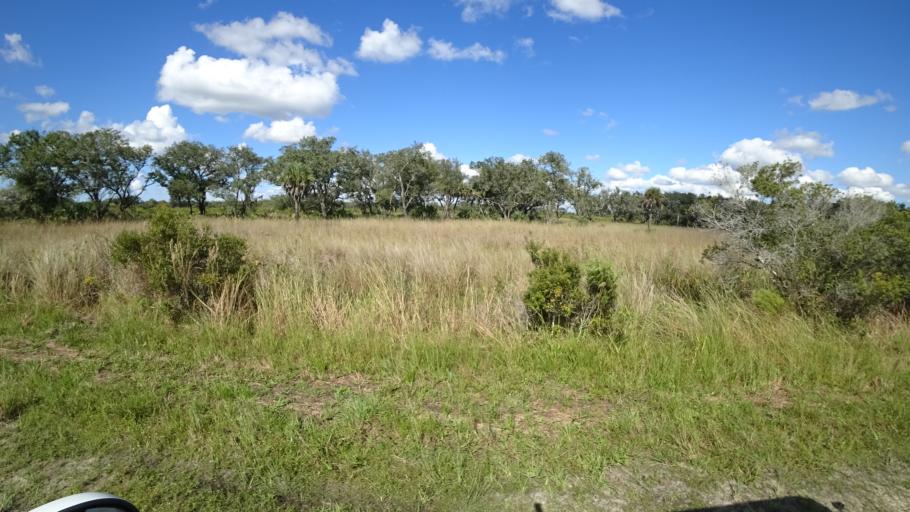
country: US
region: Florida
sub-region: Sarasota County
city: Lake Sarasota
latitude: 27.2470
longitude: -82.2809
